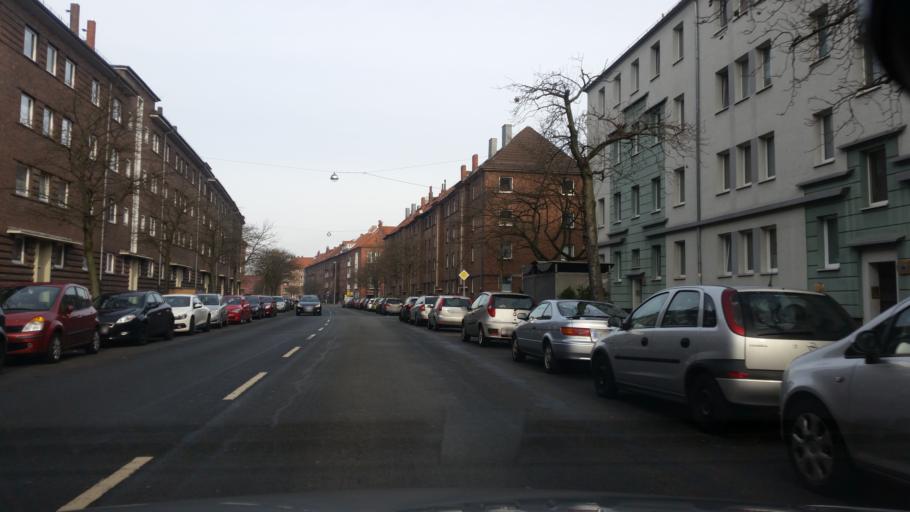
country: DE
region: Lower Saxony
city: Hannover
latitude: 52.3952
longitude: 9.7283
